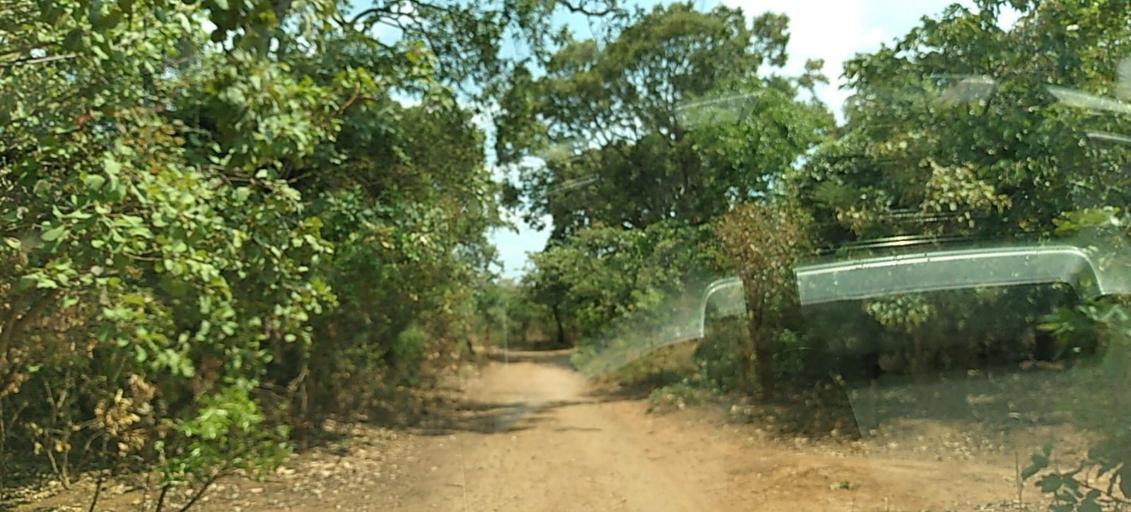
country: CD
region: Katanga
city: Kipushi
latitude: -12.0362
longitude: 27.4364
